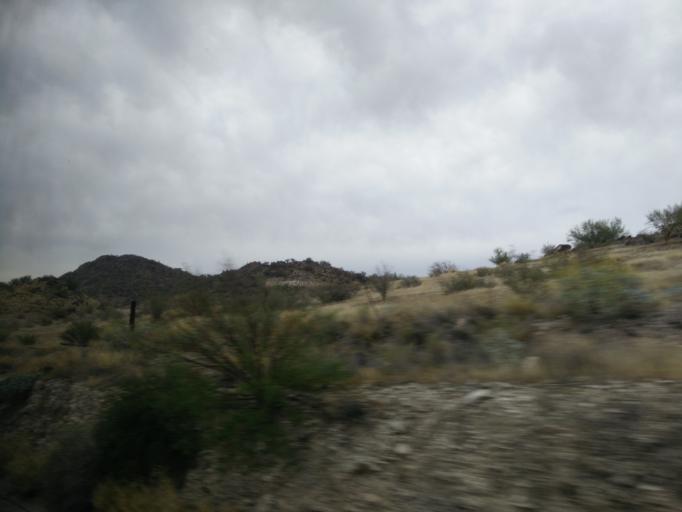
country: MX
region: Sonora
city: Hermosillo
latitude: 28.9808
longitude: -110.9657
